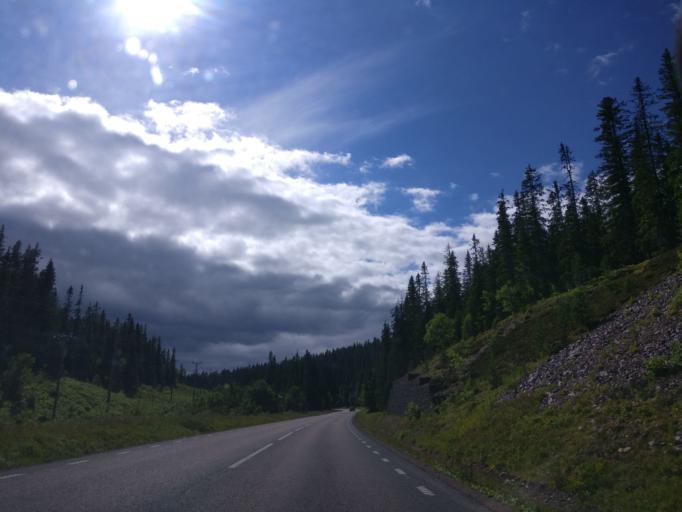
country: SE
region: Dalarna
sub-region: Malung-Saelens kommun
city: Malung
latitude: 61.1677
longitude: 13.1558
